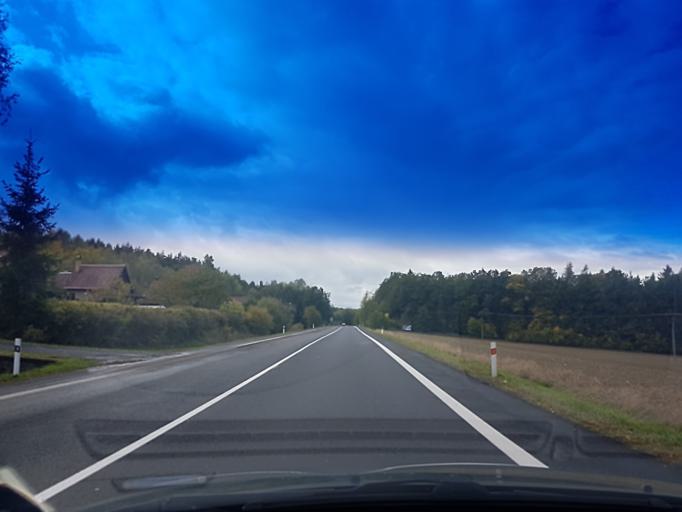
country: CZ
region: Karlovarsky
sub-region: Okres Cheb
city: Frantiskovy Lazne
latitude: 50.0813
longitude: 12.3242
